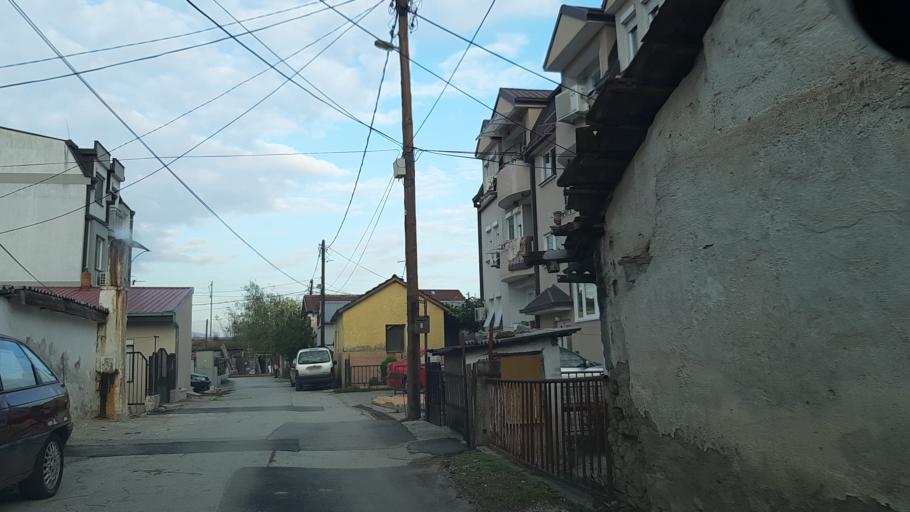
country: MK
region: Karpos
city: Skopje
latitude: 41.9827
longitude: 21.4422
